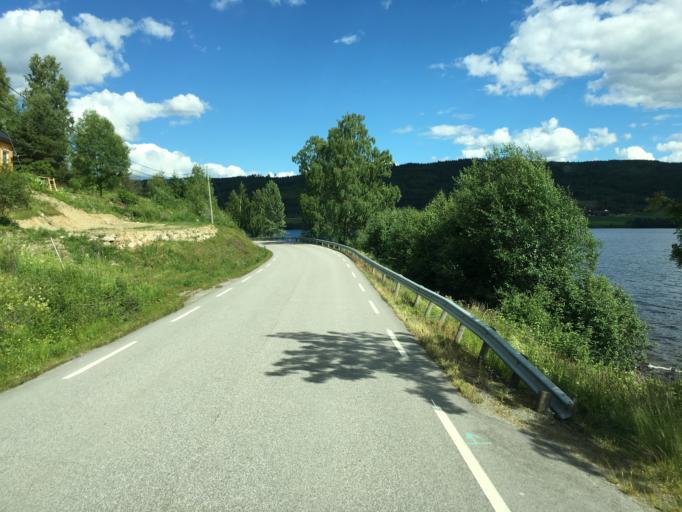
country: NO
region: Oppland
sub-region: Sondre Land
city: Hov
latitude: 60.5985
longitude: 10.3168
